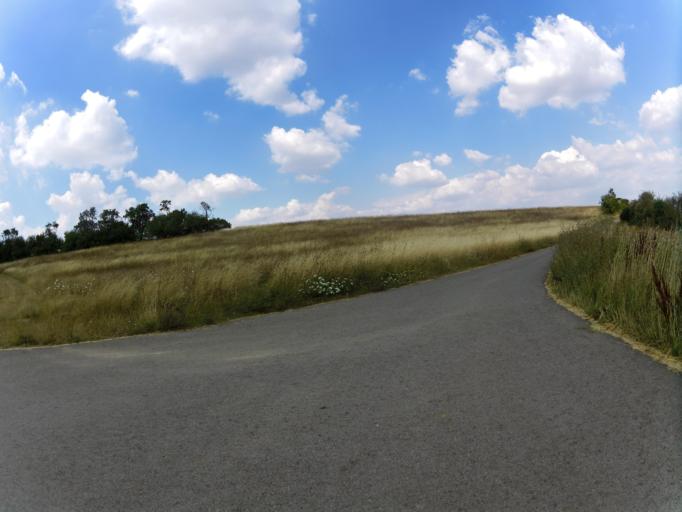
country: DE
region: Bavaria
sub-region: Regierungsbezirk Unterfranken
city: Ochsenfurt
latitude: 49.6467
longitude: 10.0728
